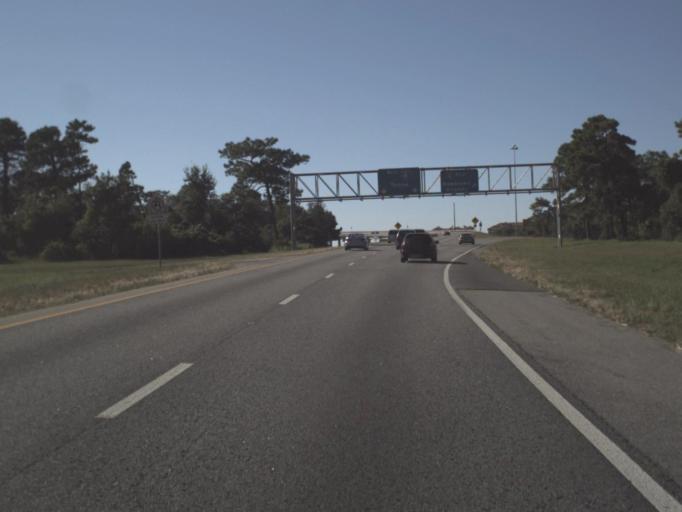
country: US
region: Florida
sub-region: Orange County
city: Williamsburg
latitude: 28.4213
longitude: -81.4697
